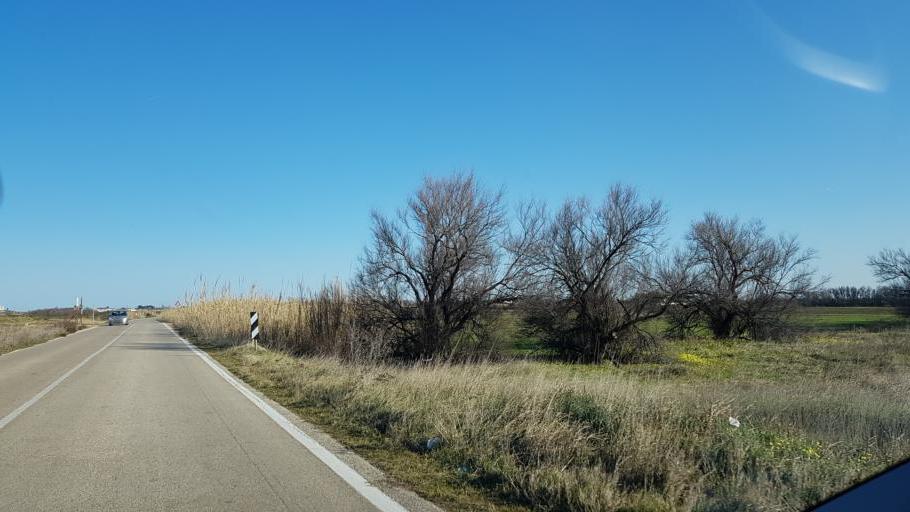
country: IT
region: Apulia
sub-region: Provincia di Brindisi
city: Brindisi
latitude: 40.6881
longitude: 17.8547
